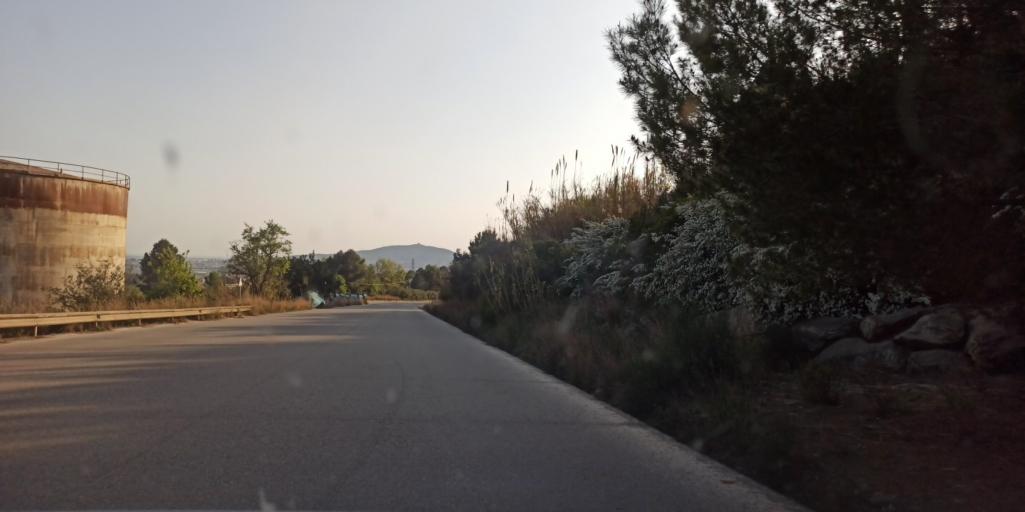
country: ES
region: Catalonia
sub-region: Provincia de Barcelona
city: Sant Feliu de Llobregat
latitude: 41.4012
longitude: 2.0564
